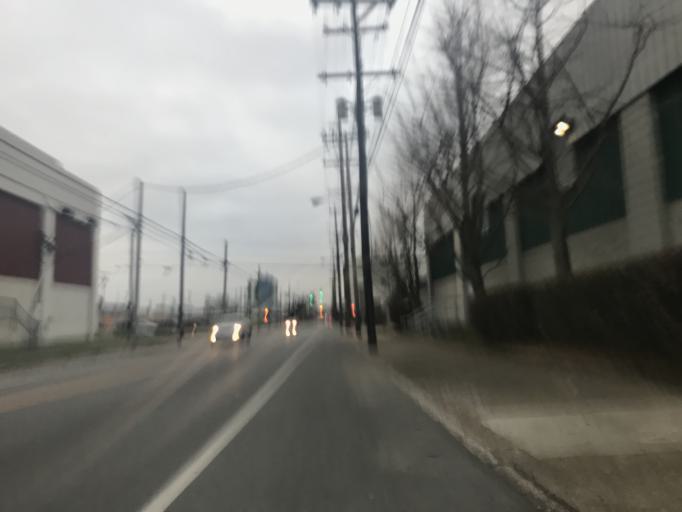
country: US
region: Kentucky
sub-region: Jefferson County
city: Louisville
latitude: 38.2372
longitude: -85.7735
